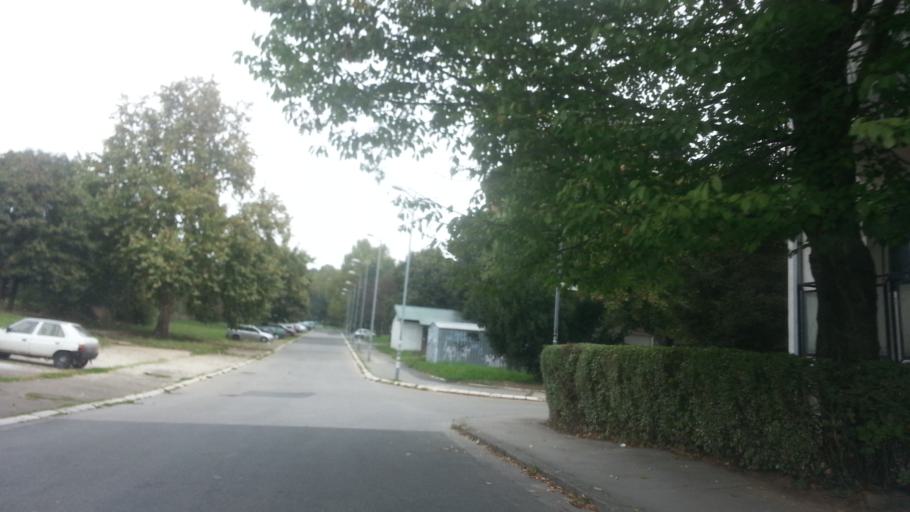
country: RS
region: Central Serbia
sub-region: Belgrade
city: Zemun
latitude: 44.8601
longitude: 20.3679
